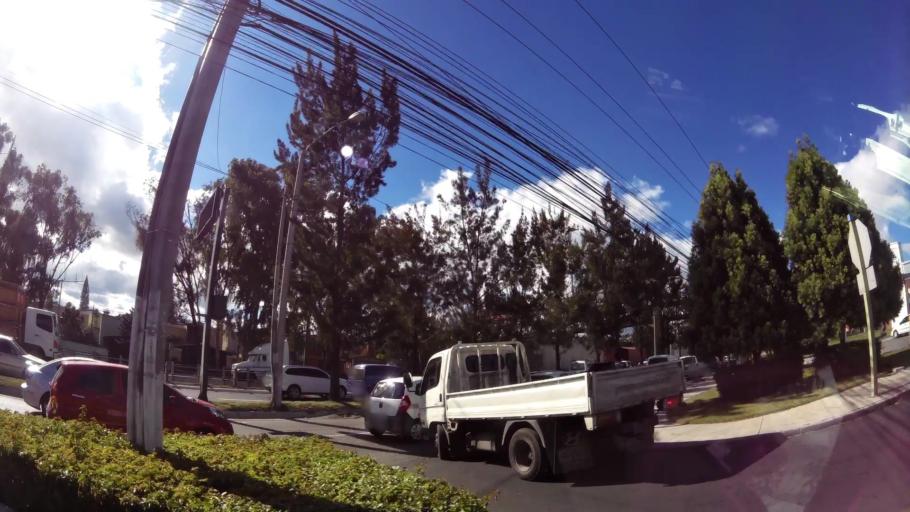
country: GT
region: Guatemala
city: Guatemala City
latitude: 14.6182
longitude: -90.5556
